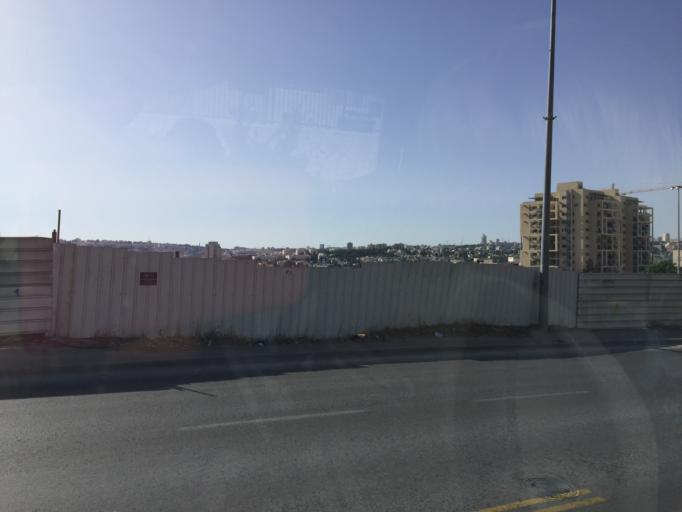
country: IL
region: Jerusalem
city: Jerusalem
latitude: 31.7438
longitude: 35.2152
